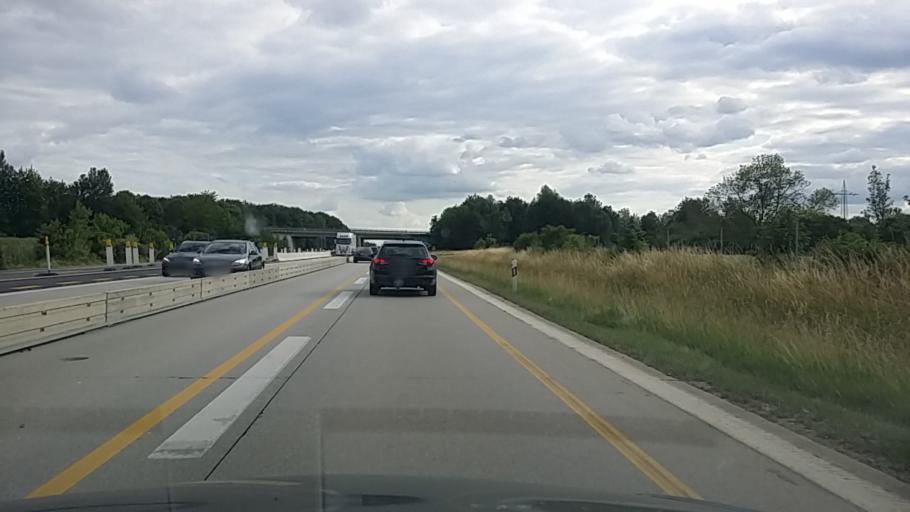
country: DE
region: Bavaria
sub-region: Upper Bavaria
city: Wang
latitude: 48.4829
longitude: 11.9936
